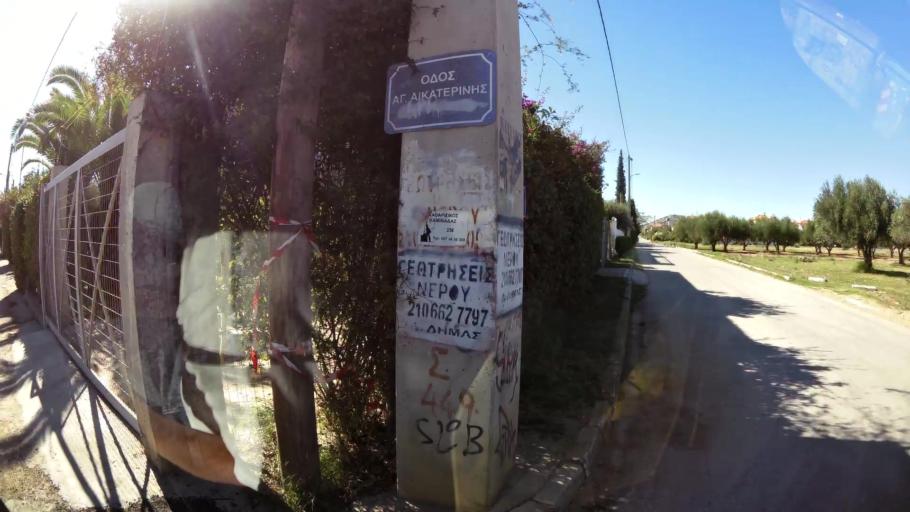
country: GR
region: Attica
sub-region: Nomarchia Anatolikis Attikis
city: Vari
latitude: 37.8354
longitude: 23.8204
